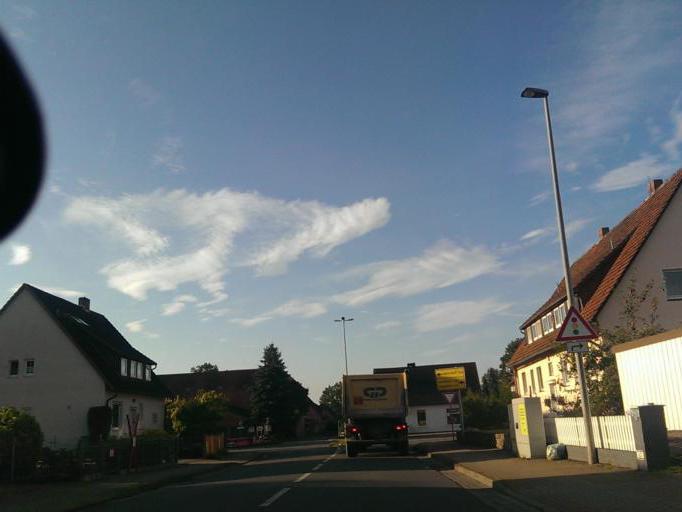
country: DE
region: Lower Saxony
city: Lindwedel
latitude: 52.5550
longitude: 9.6835
